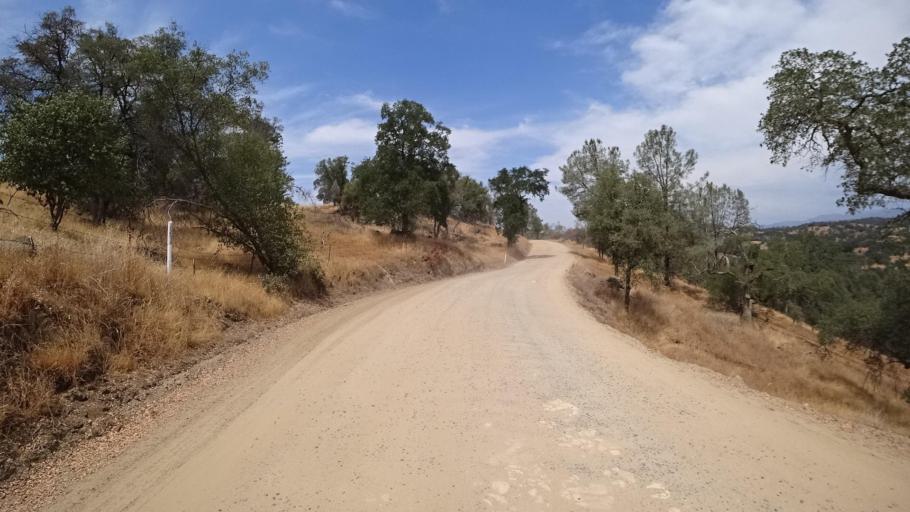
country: US
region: California
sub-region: Mariposa County
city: Mariposa
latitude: 37.3751
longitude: -119.8724
